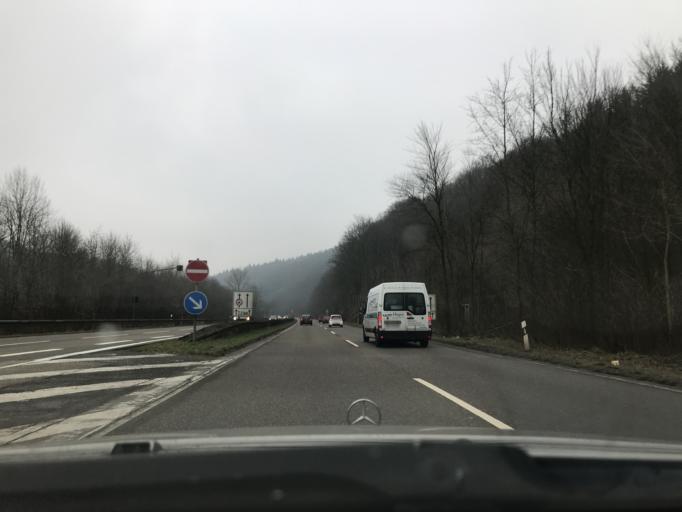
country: DE
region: North Rhine-Westphalia
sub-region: Regierungsbezirk Dusseldorf
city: Solingen
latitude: 51.1973
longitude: 7.1075
